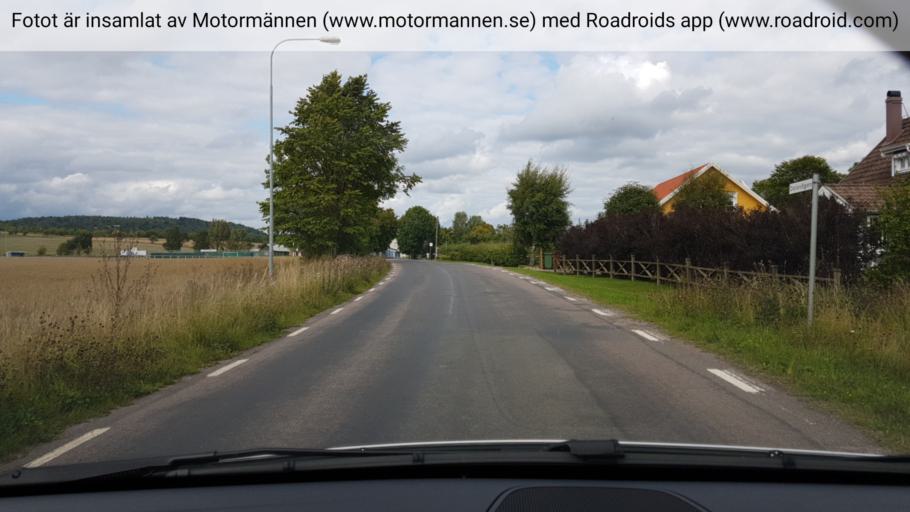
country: SE
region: Vaestra Goetaland
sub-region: Skovde Kommun
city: Skultorp
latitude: 58.2794
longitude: 13.7915
